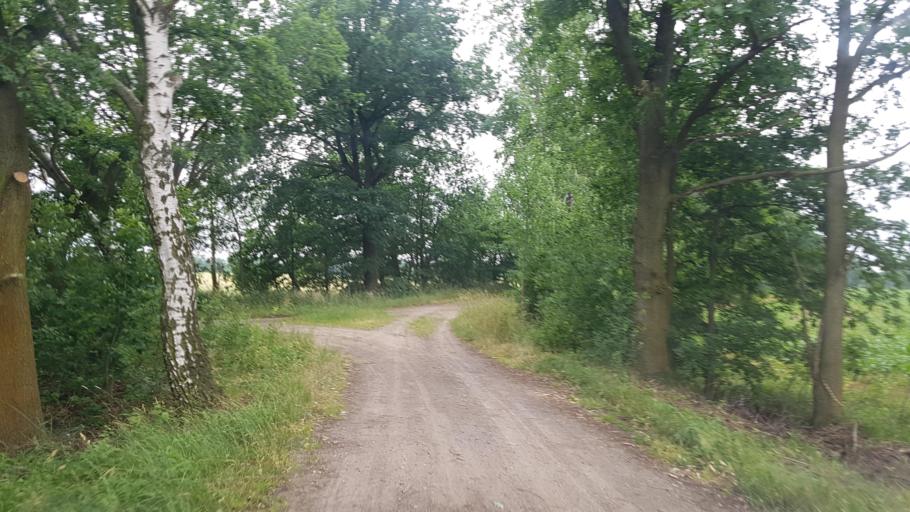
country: DE
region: Brandenburg
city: Grossthiemig
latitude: 51.4122
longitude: 13.6749
